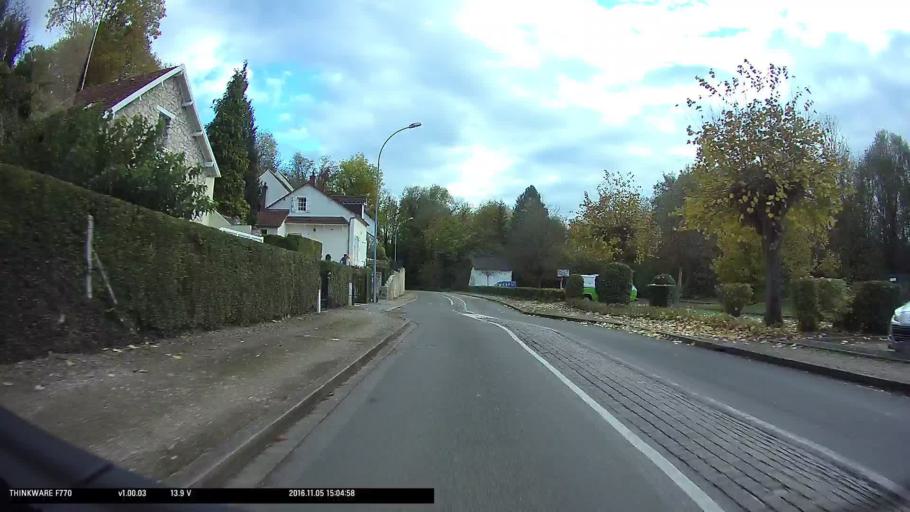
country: FR
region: Ile-de-France
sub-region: Departement du Val-d'Oise
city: Ableiges
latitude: 49.0804
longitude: 2.0080
